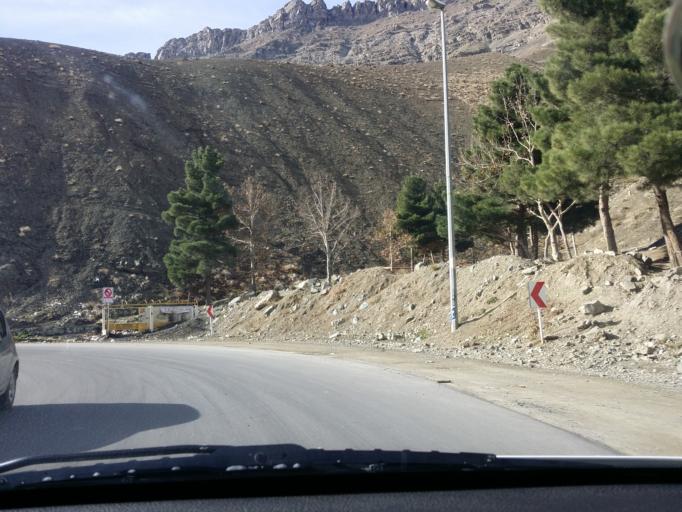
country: IR
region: Alborz
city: Karaj
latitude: 35.9730
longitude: 51.0947
